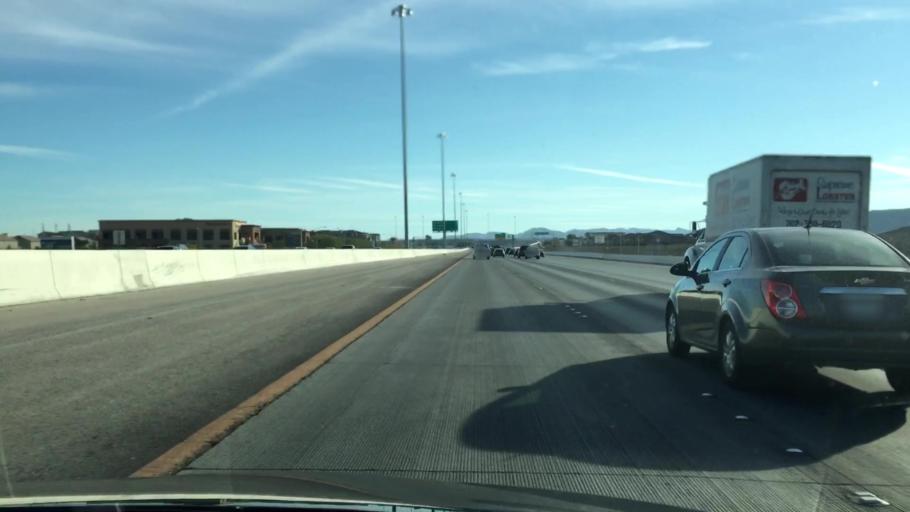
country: US
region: Nevada
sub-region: Clark County
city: Spring Valley
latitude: 36.0801
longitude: -115.2890
